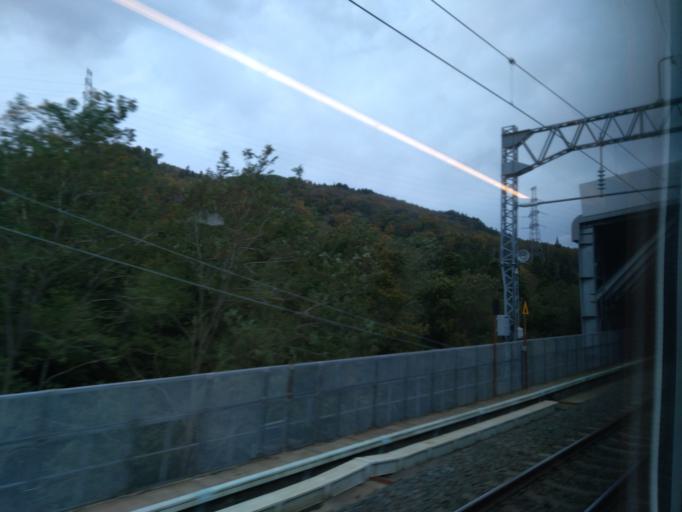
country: JP
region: Aomori
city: Goshogawara
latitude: 41.1498
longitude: 140.5113
